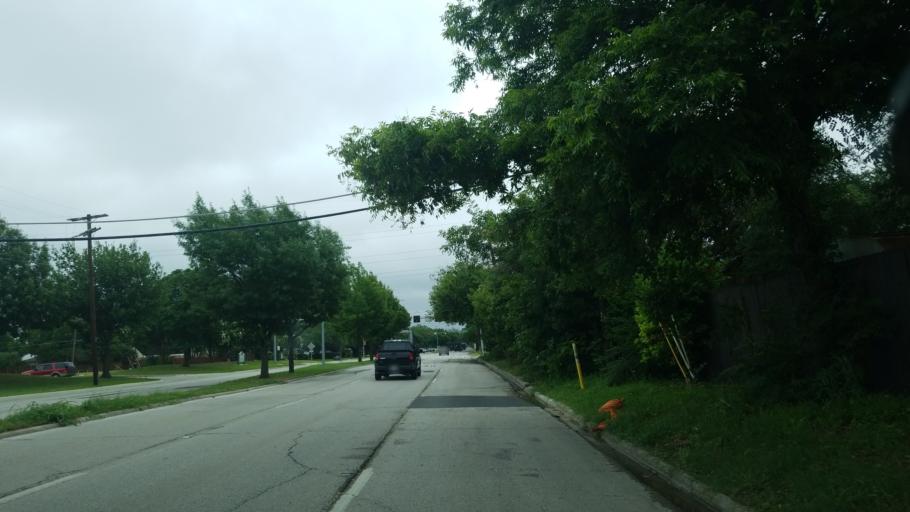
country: US
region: Texas
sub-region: Dallas County
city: Farmers Branch
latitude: 32.8951
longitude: -96.8643
